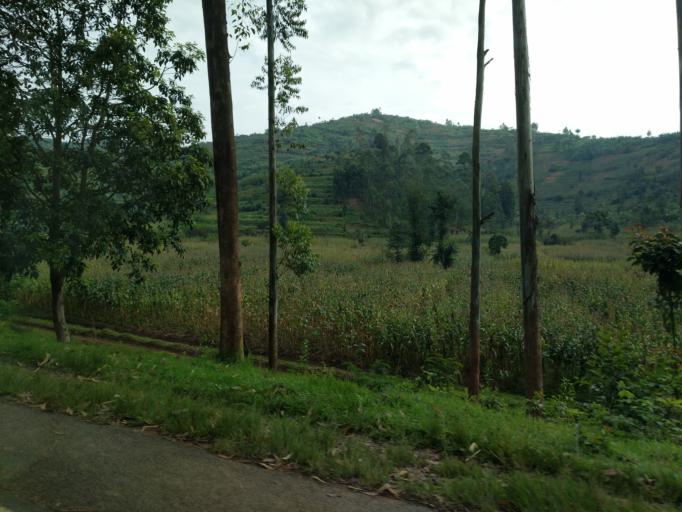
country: RW
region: Northern Province
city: Musanze
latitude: -1.5745
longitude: 29.7187
